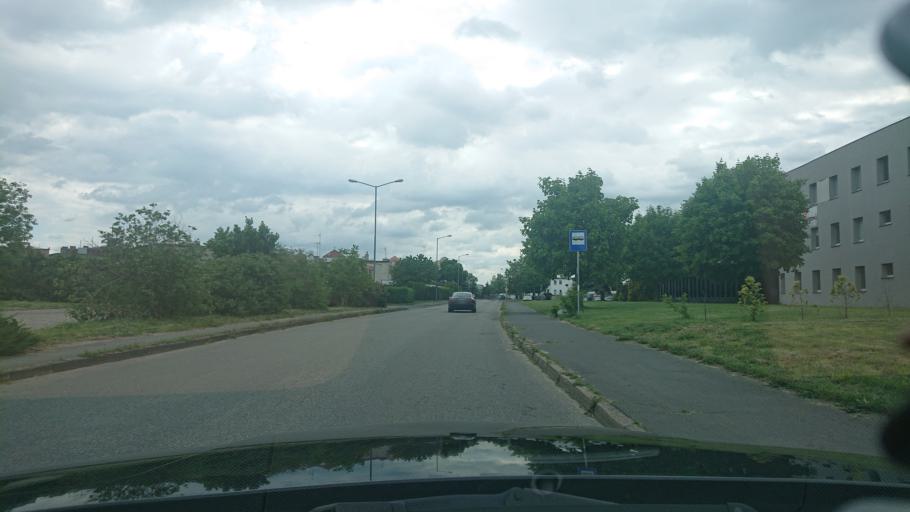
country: PL
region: Greater Poland Voivodeship
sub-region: Powiat gnieznienski
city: Gniezno
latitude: 52.5357
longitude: 17.6295
